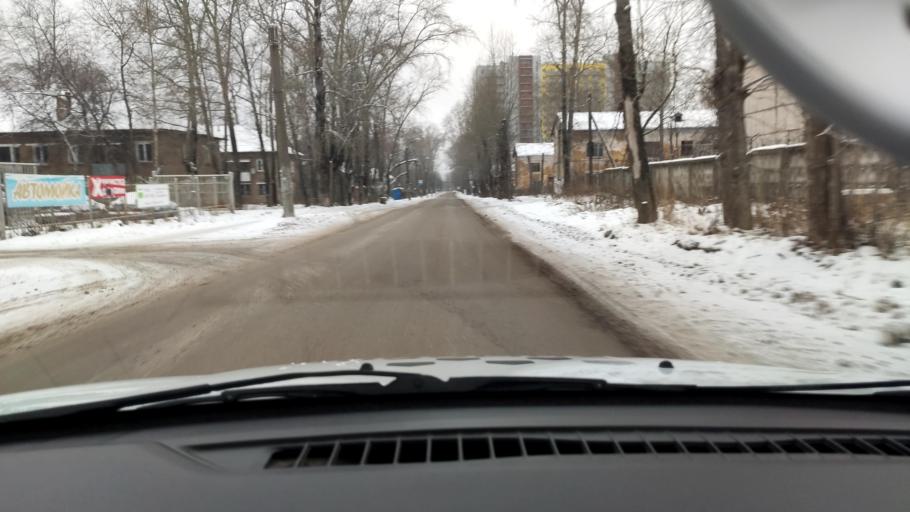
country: RU
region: Perm
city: Perm
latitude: 58.0922
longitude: 56.3805
